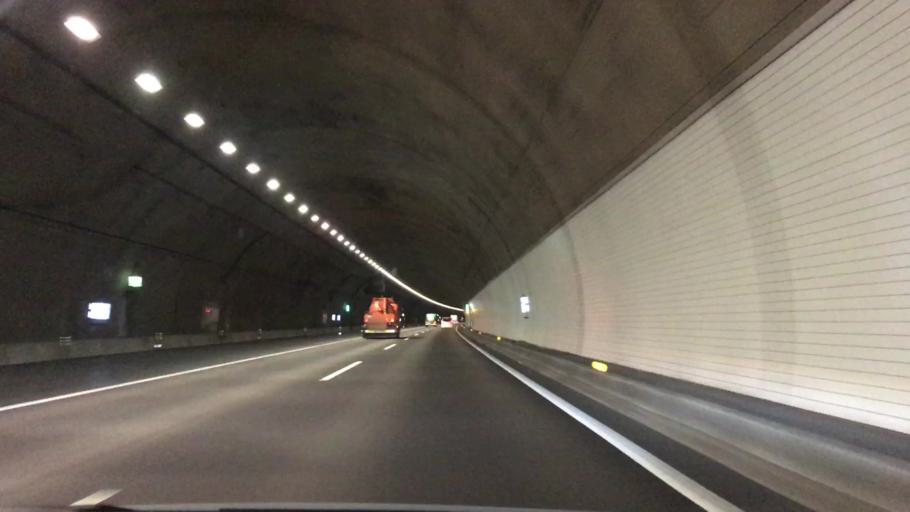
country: JP
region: Shizuoka
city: Hamakita
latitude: 34.8734
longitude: 137.6712
